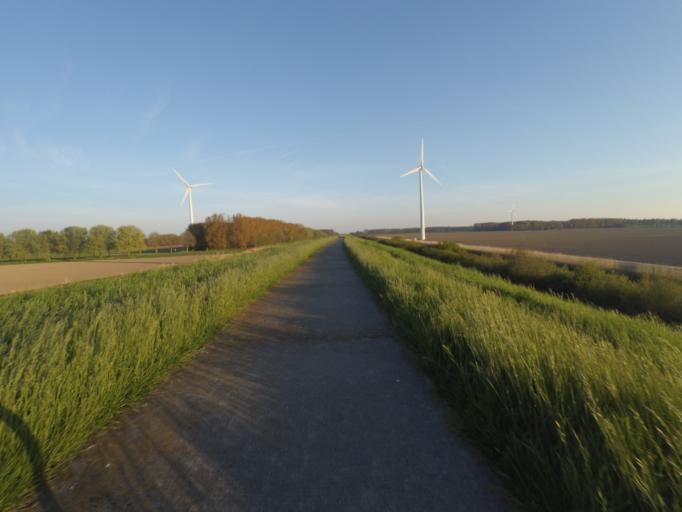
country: NL
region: Flevoland
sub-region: Gemeente Zeewolde
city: Zeewolde
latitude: 52.3980
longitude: 5.5095
